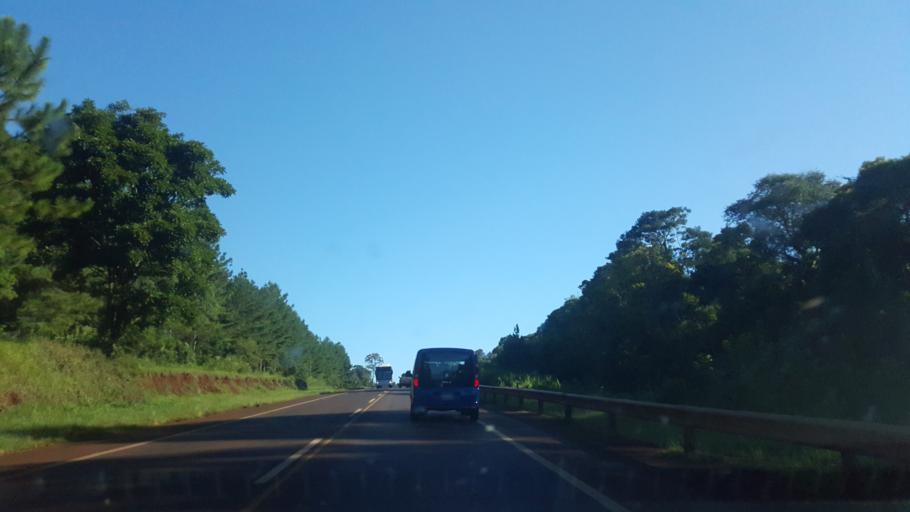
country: AR
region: Misiones
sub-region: Departamento de Eldorado
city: Eldorado
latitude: -26.2158
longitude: -54.5876
